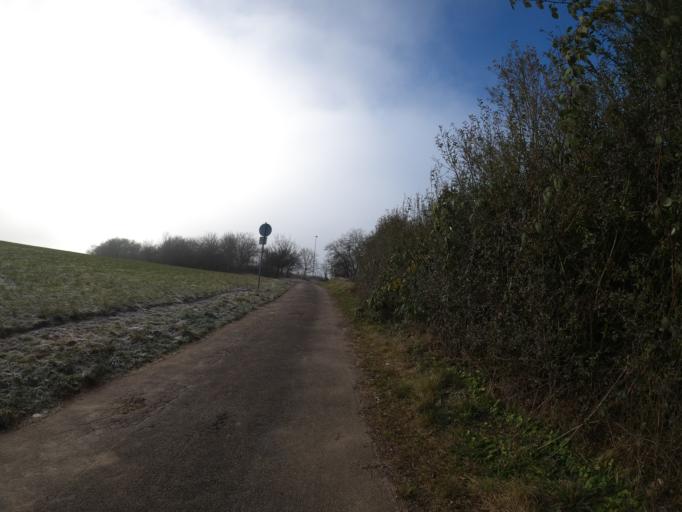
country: DE
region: Baden-Wuerttemberg
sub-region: Regierungsbezirk Stuttgart
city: Bad Uberkingen
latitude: 48.5856
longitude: 9.7738
